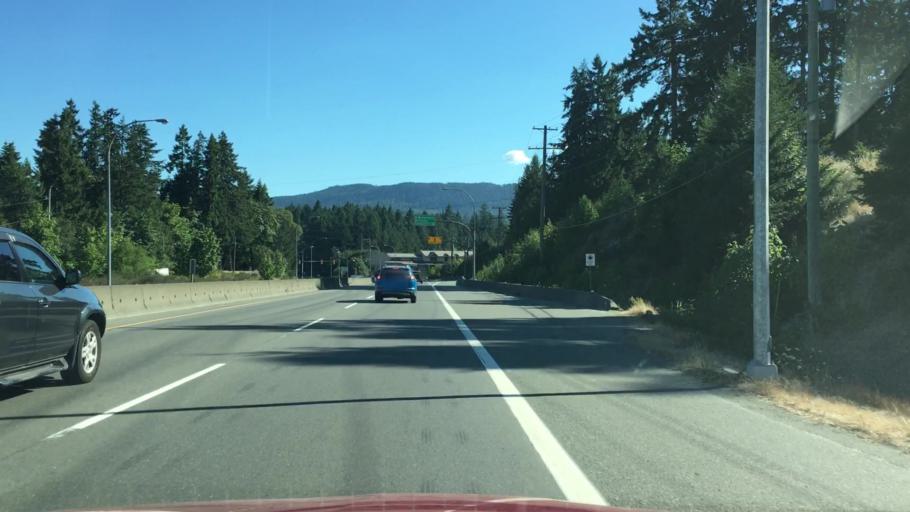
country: CA
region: British Columbia
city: North Saanich
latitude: 48.6599
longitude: -123.5603
